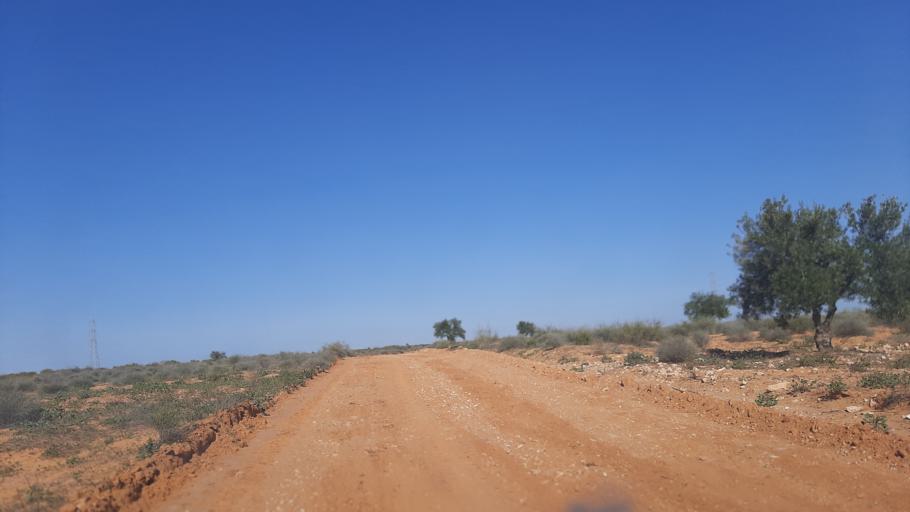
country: TN
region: Madanin
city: Medenine
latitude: 33.2754
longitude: 10.7718
